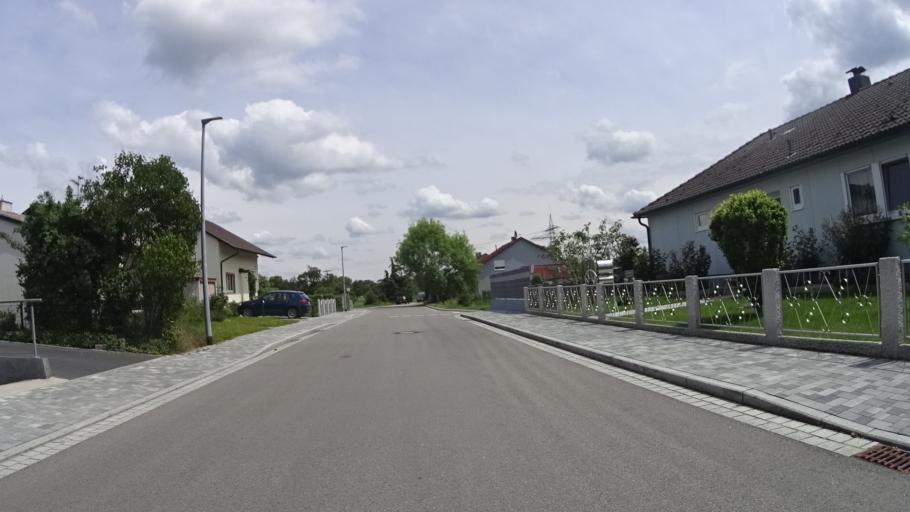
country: DE
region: Baden-Wuerttemberg
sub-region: Freiburg Region
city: Grenzach-Wyhlen
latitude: 47.5427
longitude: 7.7019
